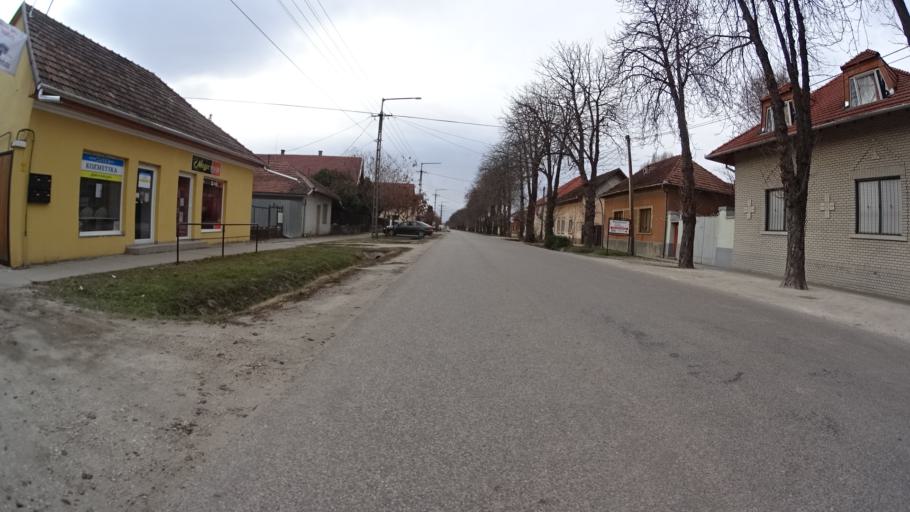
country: HU
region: Bacs-Kiskun
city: Tiszakecske
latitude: 46.9336
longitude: 20.0942
